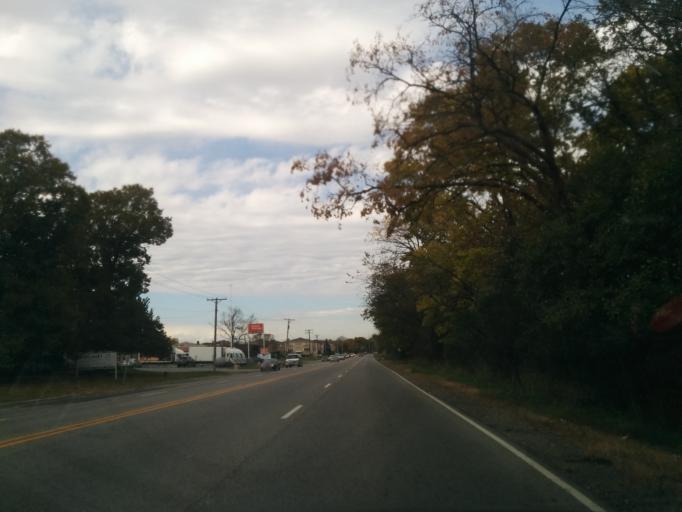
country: US
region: Illinois
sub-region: Cook County
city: Franklin Park
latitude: 41.9485
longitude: -87.8559
